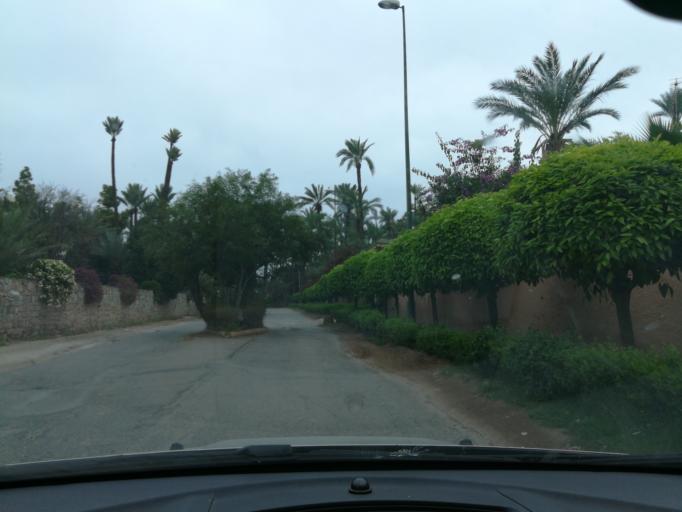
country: MA
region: Marrakech-Tensift-Al Haouz
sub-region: Marrakech
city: Marrakesh
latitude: 31.6541
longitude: -7.9792
